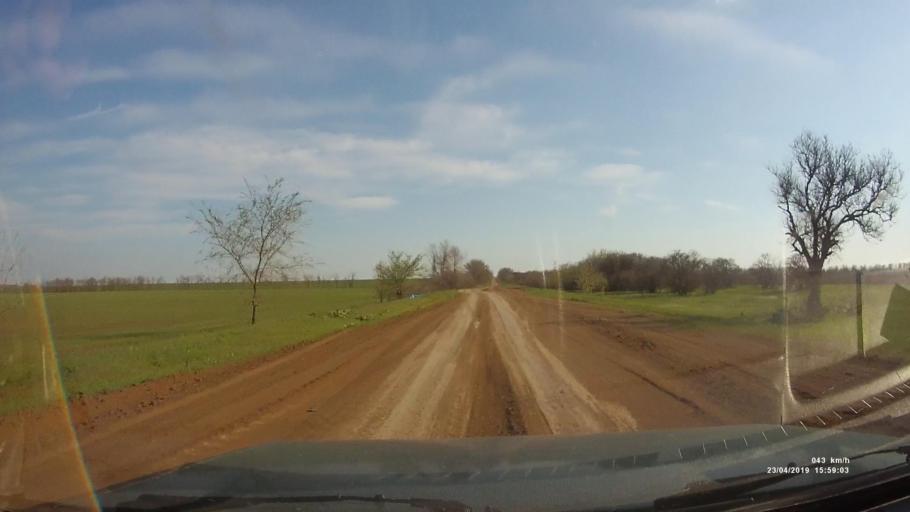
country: RU
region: Rostov
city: Remontnoye
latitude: 46.5194
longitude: 43.1096
